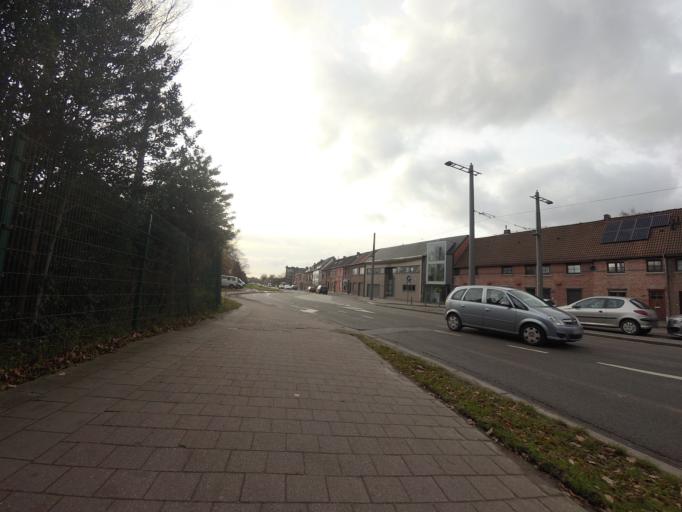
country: BE
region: Flanders
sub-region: Provincie Antwerpen
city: Hoboken
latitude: 51.1686
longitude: 4.3628
